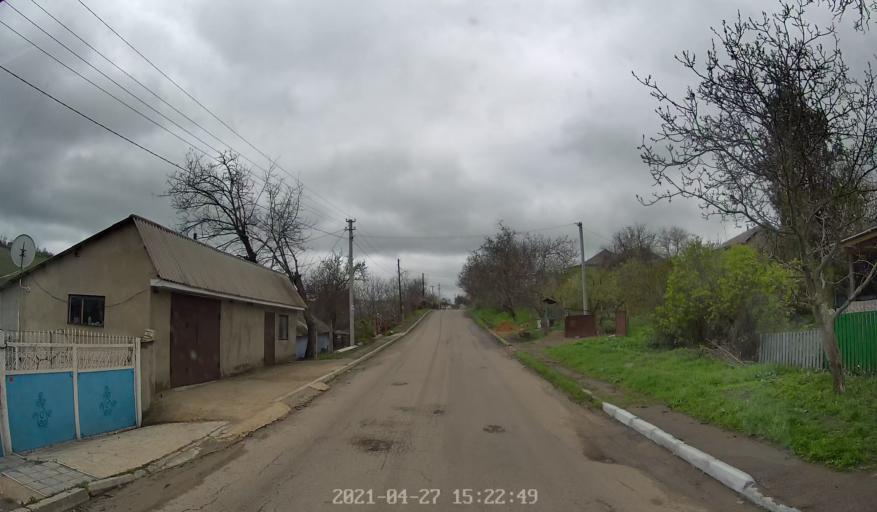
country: MD
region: Chisinau
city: Vadul lui Voda
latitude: 47.0264
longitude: 29.0248
